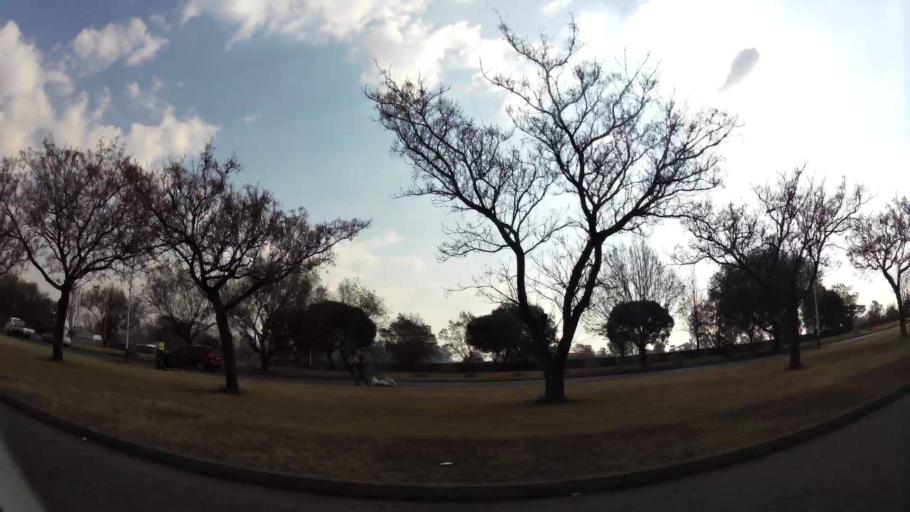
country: ZA
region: Gauteng
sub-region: Ekurhuleni Metropolitan Municipality
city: Boksburg
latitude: -26.2324
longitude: 28.2485
